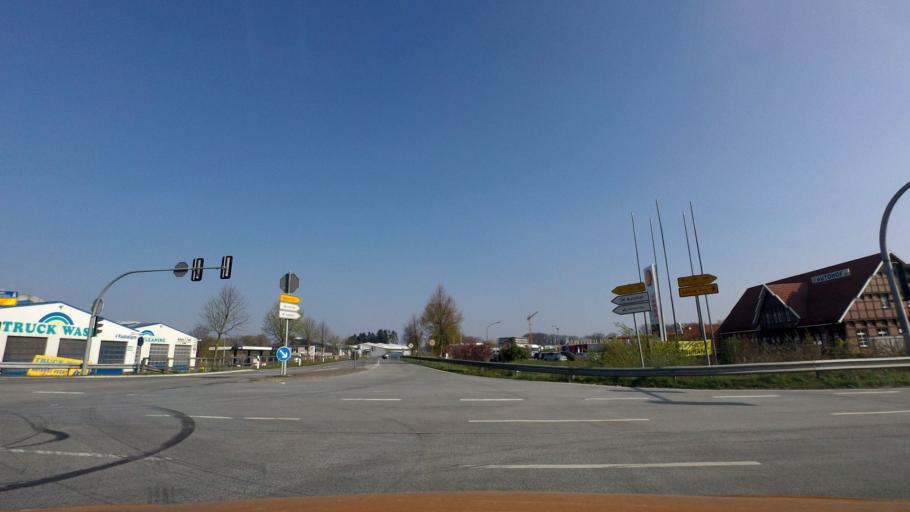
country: DE
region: Lower Saxony
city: Bakum
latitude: 52.7251
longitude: 8.1780
